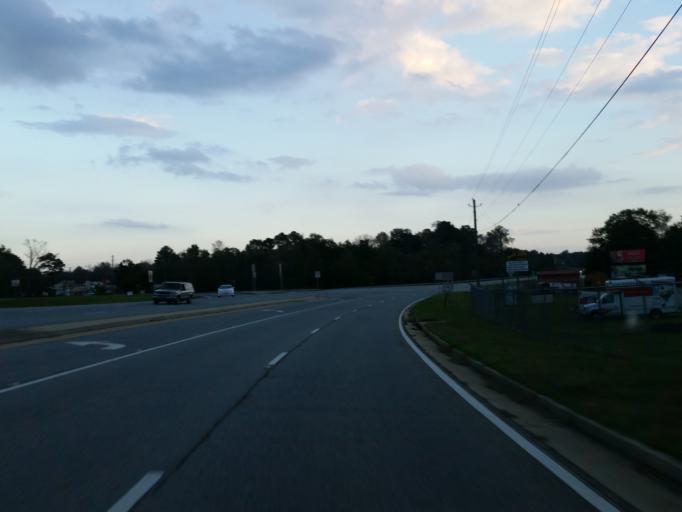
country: US
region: Georgia
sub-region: Pulaski County
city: Hawkinsville
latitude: 32.2937
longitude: -83.4832
